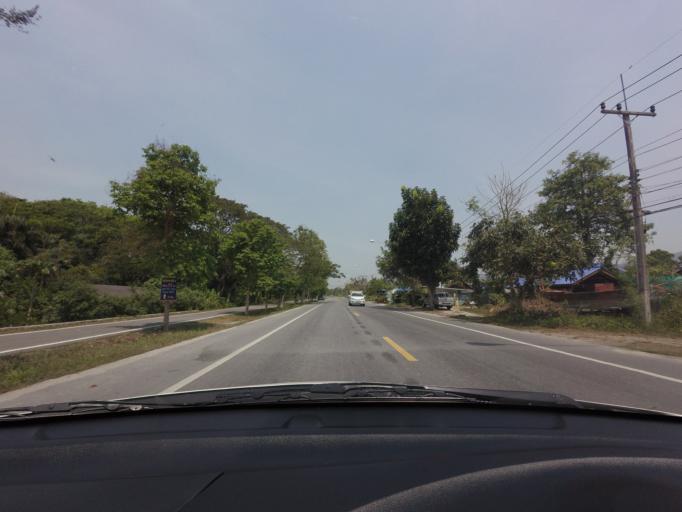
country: TH
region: Chon Buri
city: Si Racha
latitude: 13.2245
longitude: 100.9997
